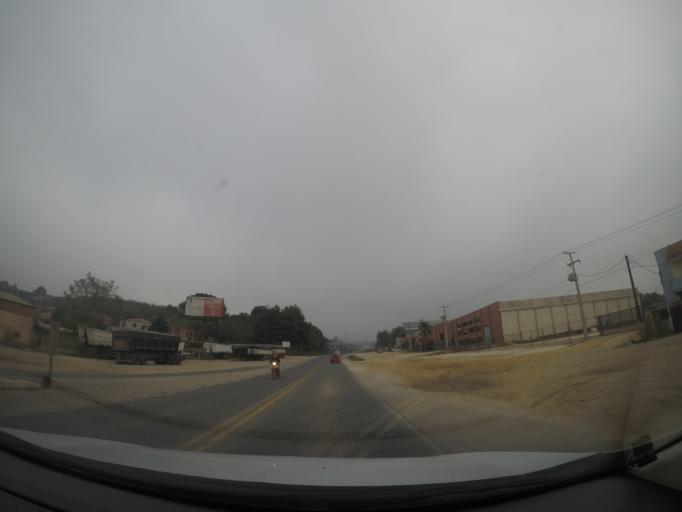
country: BR
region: Parana
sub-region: Almirante Tamandare
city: Almirante Tamandare
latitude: -25.3231
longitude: -49.2981
